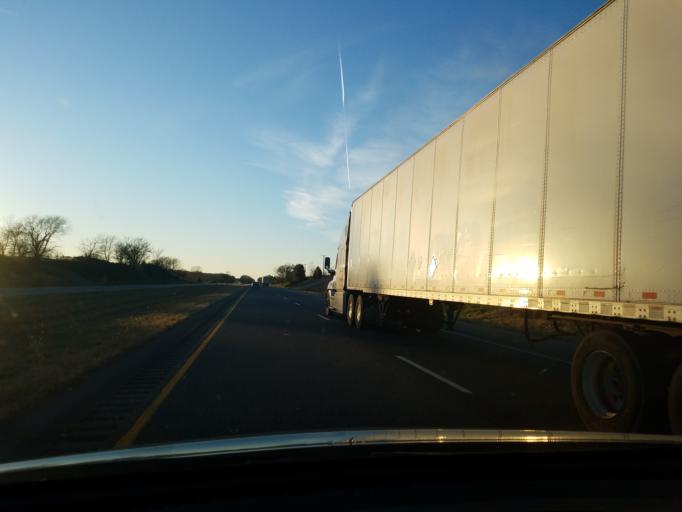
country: US
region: Indiana
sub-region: Gibson County
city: Haubstadt
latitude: 38.1671
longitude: -87.5897
